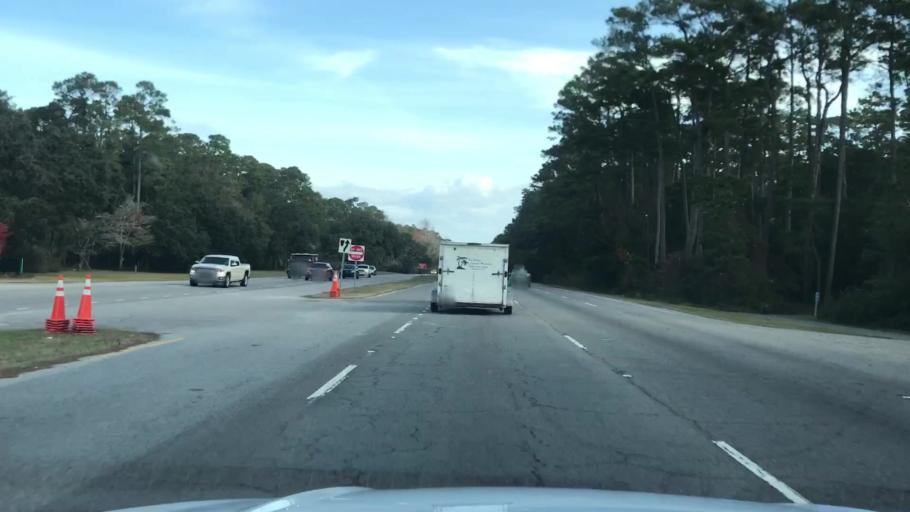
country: US
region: South Carolina
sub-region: Georgetown County
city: Murrells Inlet
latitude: 33.5089
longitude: -79.0768
